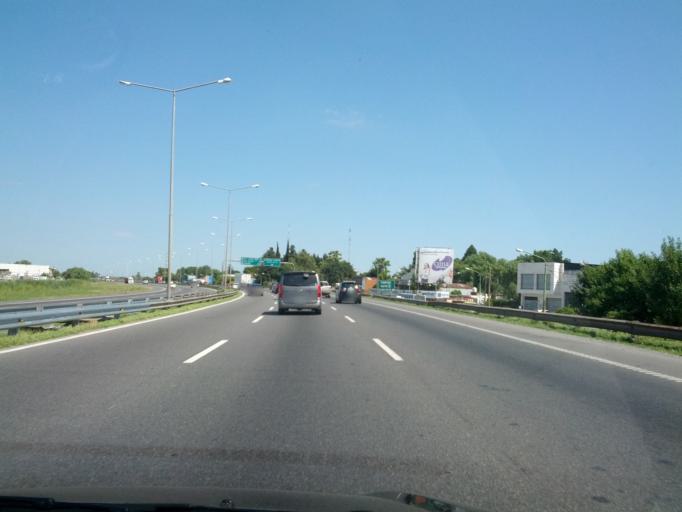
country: AR
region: Buenos Aires
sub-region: Partido de Campana
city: Campana
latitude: -34.1823
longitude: -58.9514
